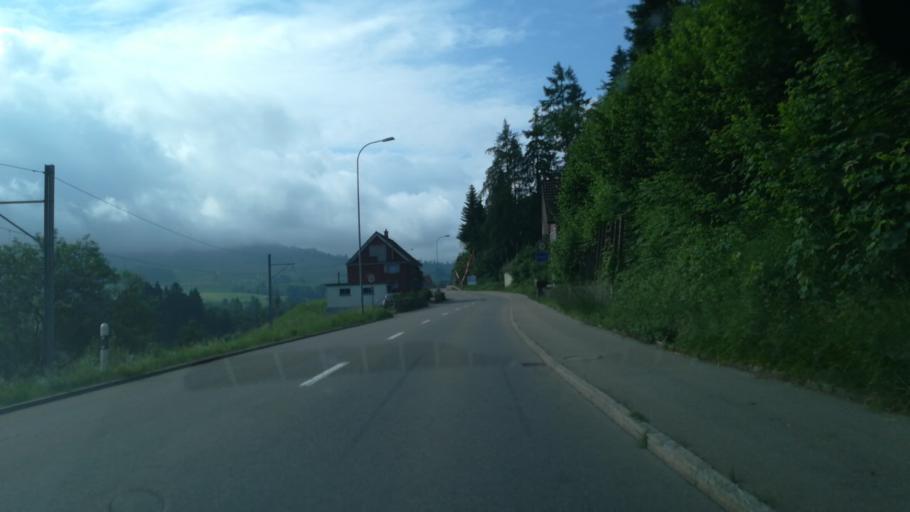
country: CH
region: Appenzell Ausserrhoden
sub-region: Bezirk Hinterland
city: Waldstatt
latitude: 47.3623
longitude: 9.2887
